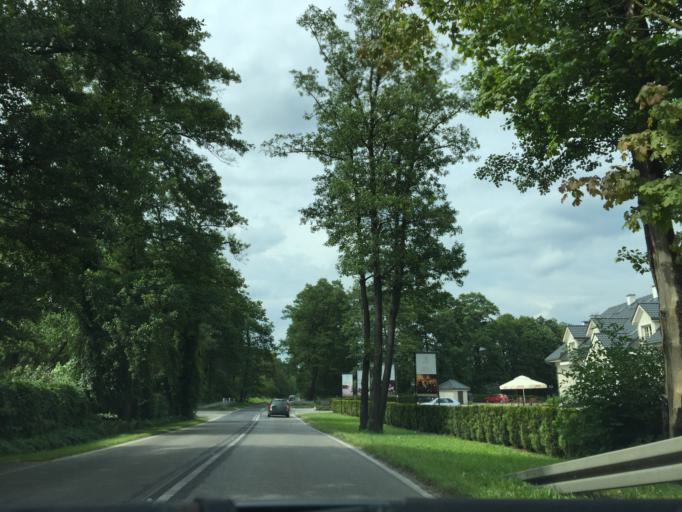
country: PL
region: Lesser Poland Voivodeship
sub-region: Powiat olkuski
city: Klucze
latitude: 50.3557
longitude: 19.5619
